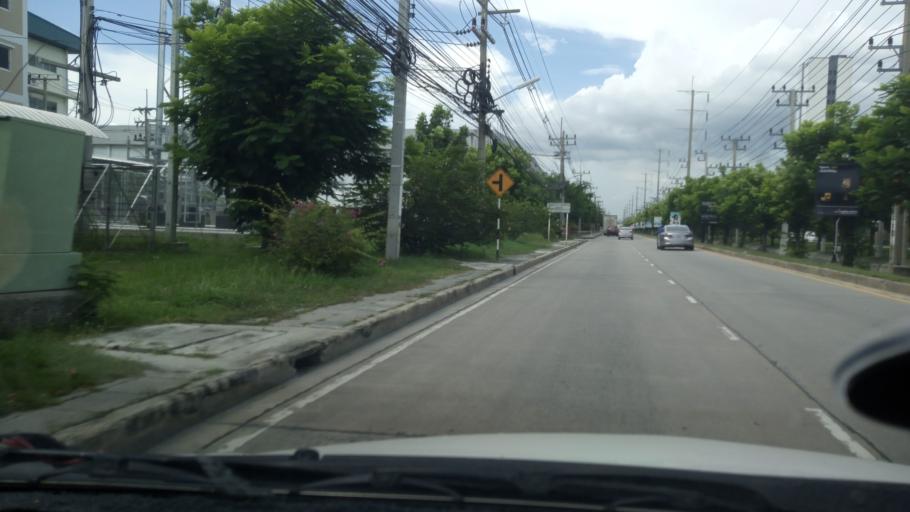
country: TH
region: Chon Buri
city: Phan Thong
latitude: 13.4371
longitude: 101.0228
